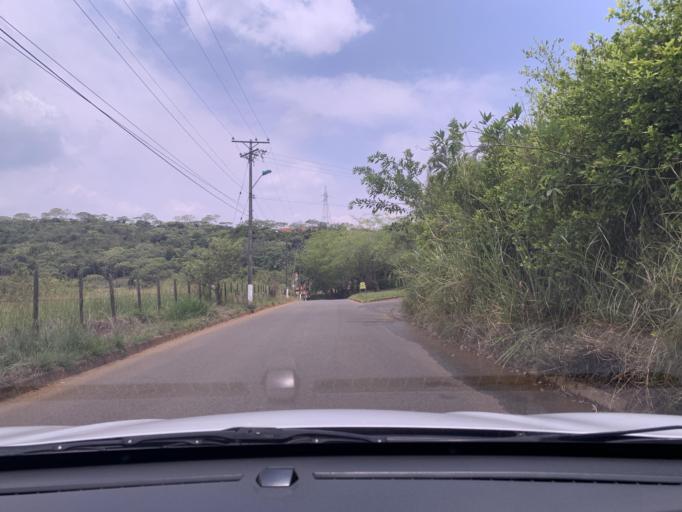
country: CO
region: Valle del Cauca
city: Jamundi
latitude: 3.3382
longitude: -76.5531
